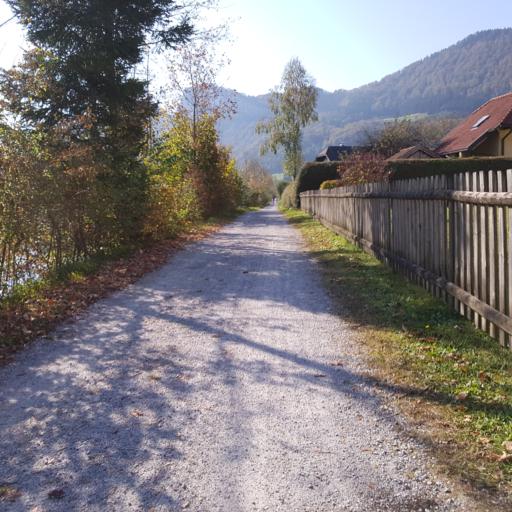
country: AT
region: Salzburg
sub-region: Politischer Bezirk Hallein
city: Puch bei Hallein
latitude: 47.7095
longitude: 13.0781
